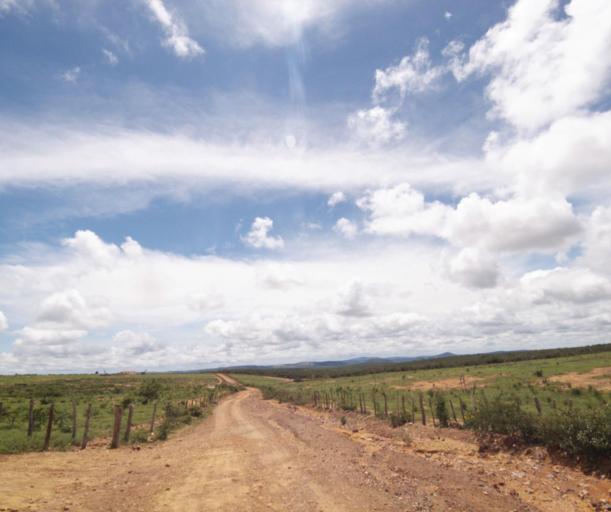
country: BR
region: Bahia
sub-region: Tanhacu
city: Tanhacu
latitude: -14.1927
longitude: -41.0589
